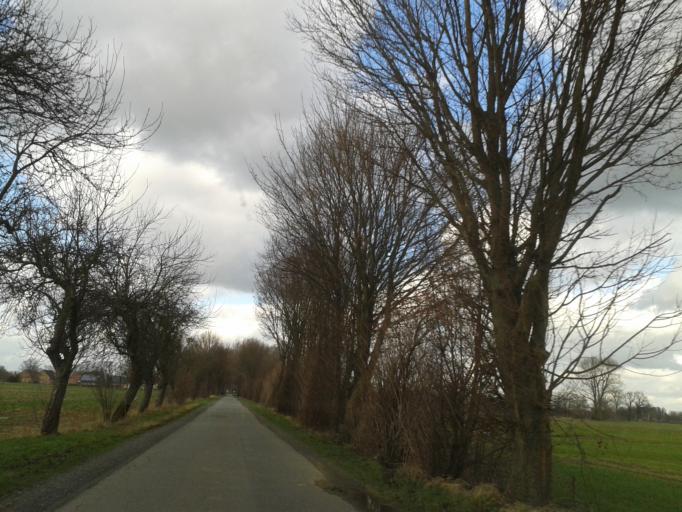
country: DE
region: North Rhine-Westphalia
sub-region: Regierungsbezirk Detmold
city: Salzkotten
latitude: 51.7300
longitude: 8.6331
